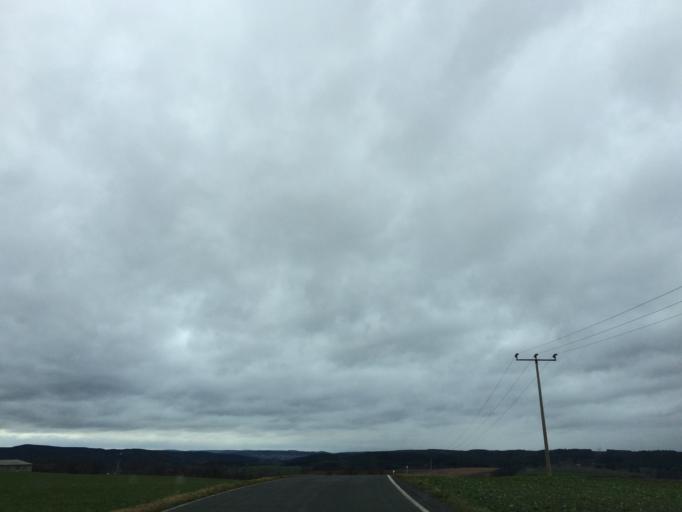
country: DE
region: Thuringia
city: Solkwitz
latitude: 50.7018
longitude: 11.6699
